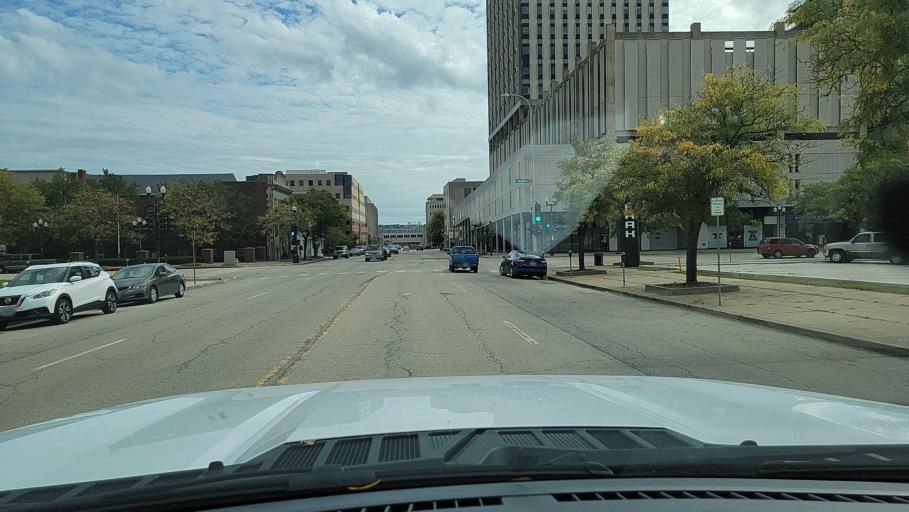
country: US
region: Illinois
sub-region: Peoria County
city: Peoria
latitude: 40.6950
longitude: -89.5908
